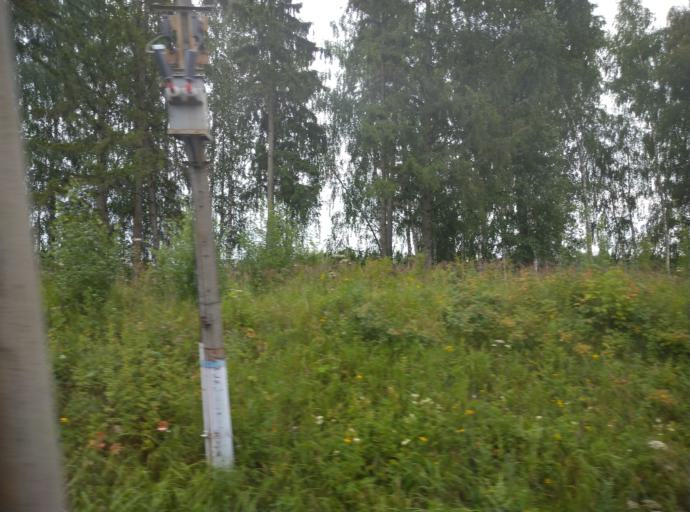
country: RU
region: Kostroma
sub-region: Kostromskoy Rayon
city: Kostroma
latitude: 57.7326
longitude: 40.9341
